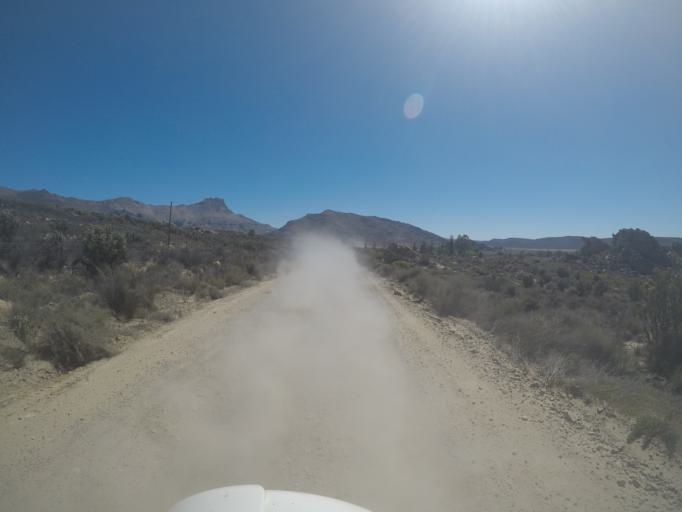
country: ZA
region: Western Cape
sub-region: Cape Winelands District Municipality
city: Ceres
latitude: -32.8724
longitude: 19.4446
